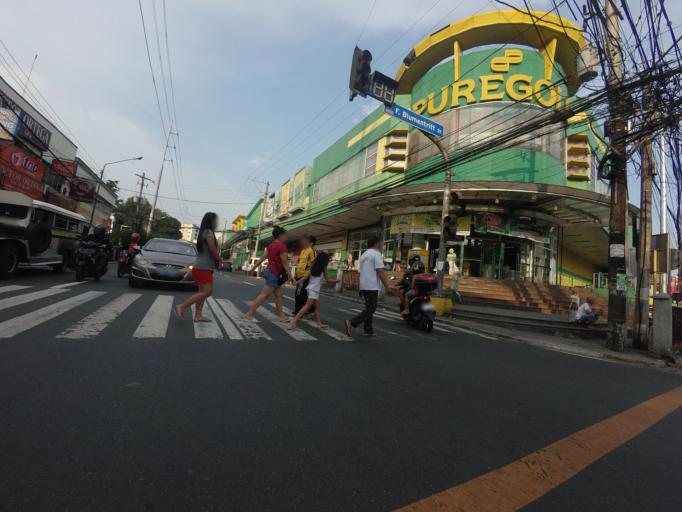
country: PH
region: Metro Manila
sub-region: San Juan
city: San Juan
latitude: 14.6048
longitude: 121.0225
